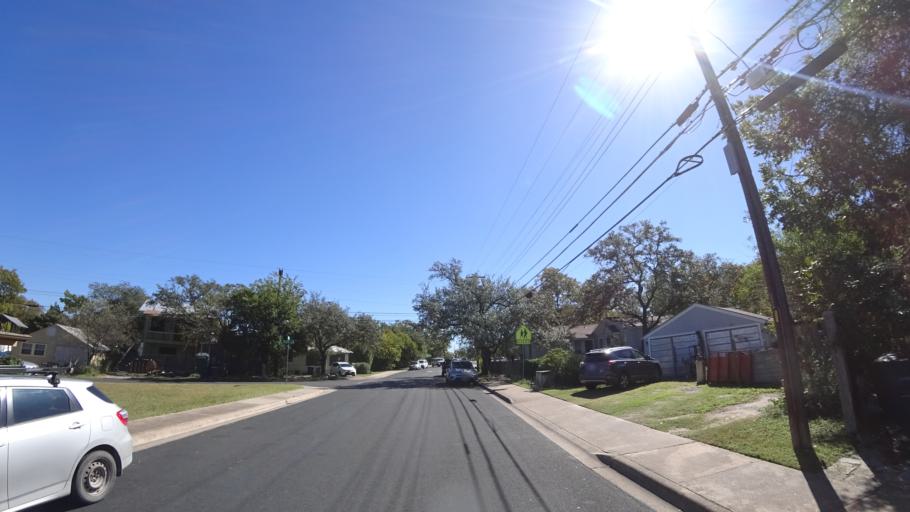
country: US
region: Texas
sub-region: Travis County
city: Austin
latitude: 30.3211
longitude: -97.7414
